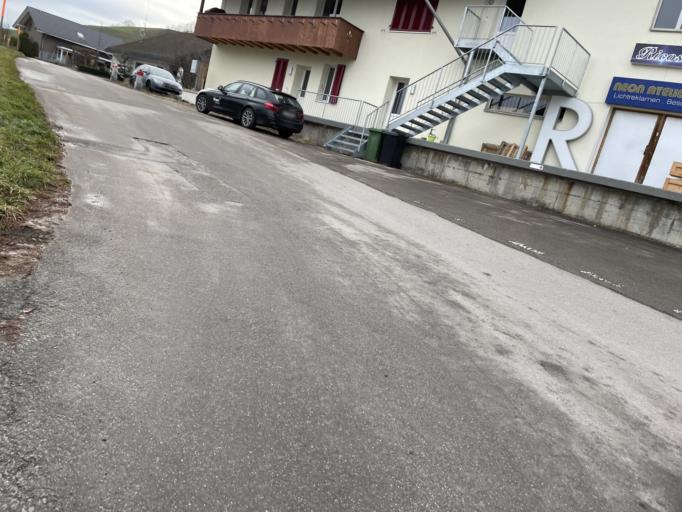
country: CH
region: Bern
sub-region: Bern-Mittelland District
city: Munsingen
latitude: 46.8665
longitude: 7.5277
